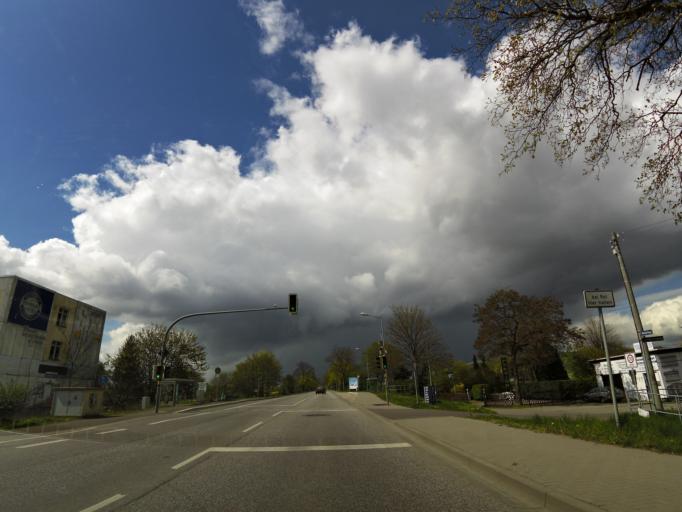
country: DE
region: Saxony-Anhalt
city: Biederitz
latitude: 52.1325
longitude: 11.6942
